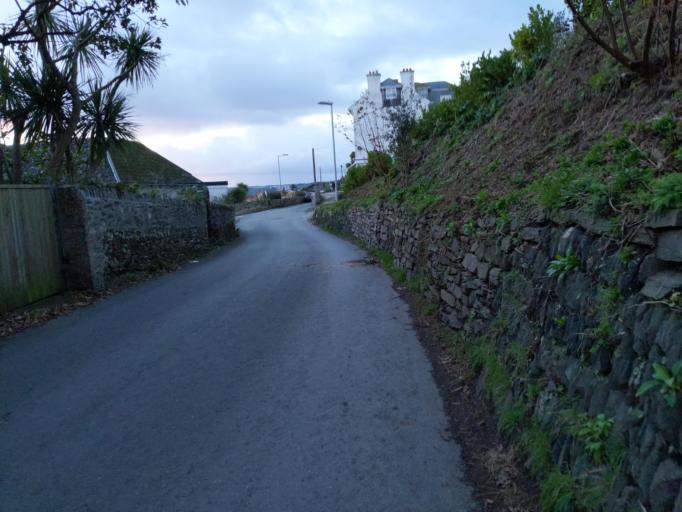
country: GB
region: England
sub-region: Cornwall
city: Looe
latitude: 50.3625
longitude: -4.3736
